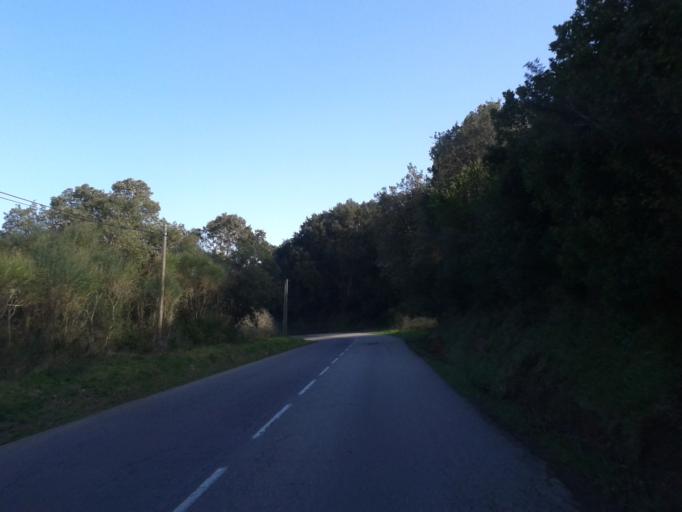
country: FR
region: Corsica
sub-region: Departement de la Haute-Corse
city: Biguglia
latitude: 42.5964
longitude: 9.4232
